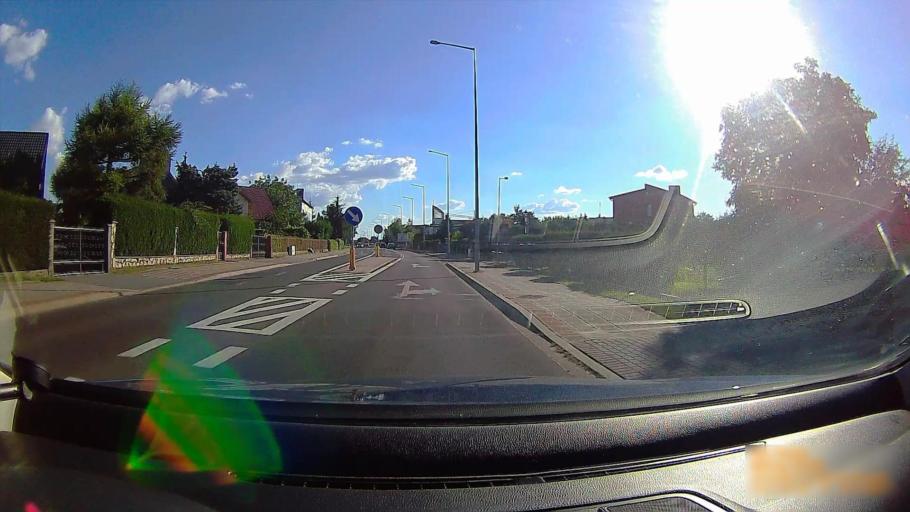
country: PL
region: Greater Poland Voivodeship
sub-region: Konin
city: Konin
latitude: 52.2007
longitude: 18.2443
